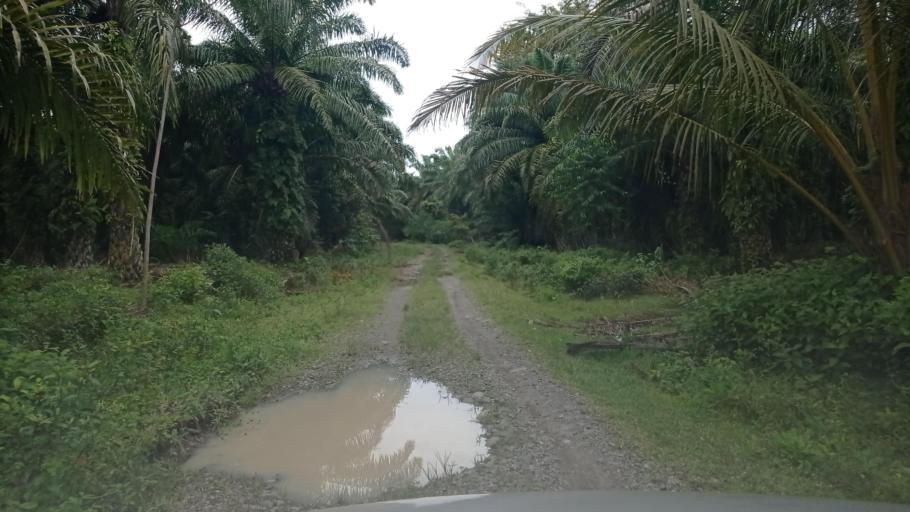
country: ID
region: Jambi
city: Sungai Penuh
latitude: -2.5136
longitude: 101.0729
